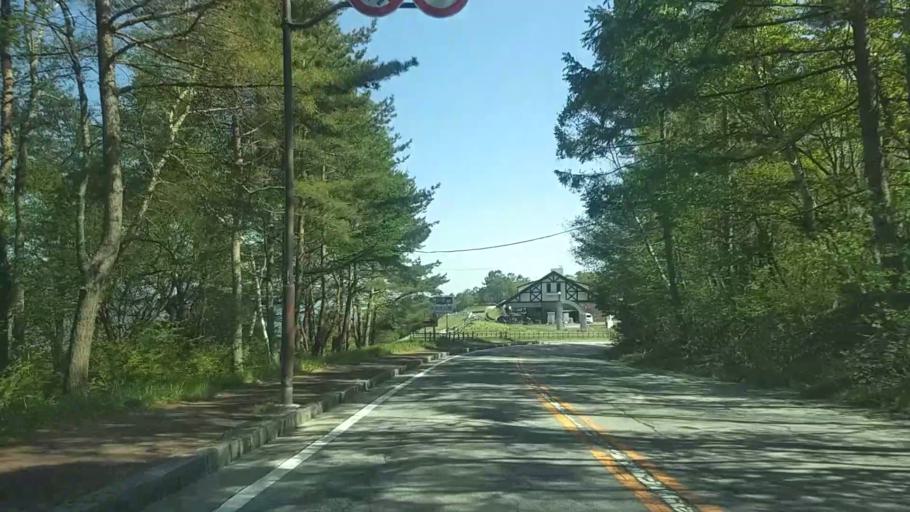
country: JP
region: Yamanashi
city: Nirasaki
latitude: 35.9248
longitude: 138.4078
